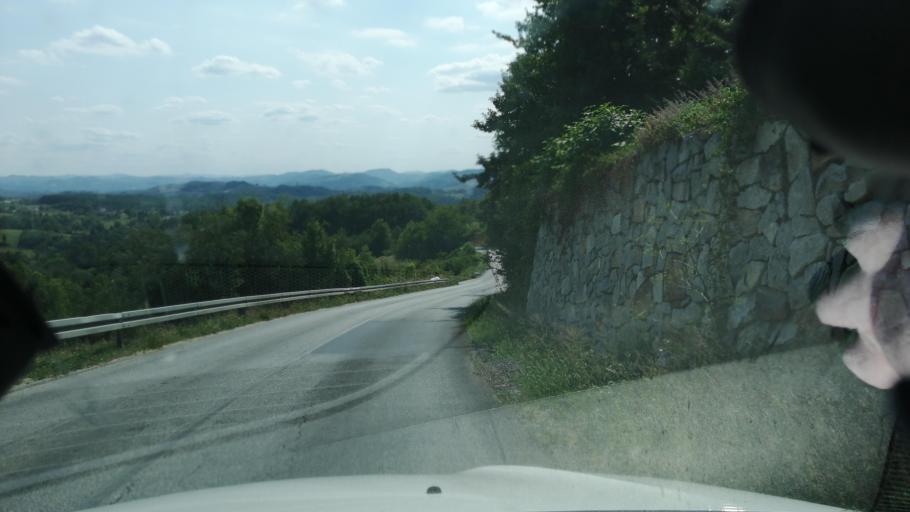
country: RS
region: Central Serbia
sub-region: Moravicki Okrug
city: Cacak
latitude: 43.8176
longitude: 20.2779
